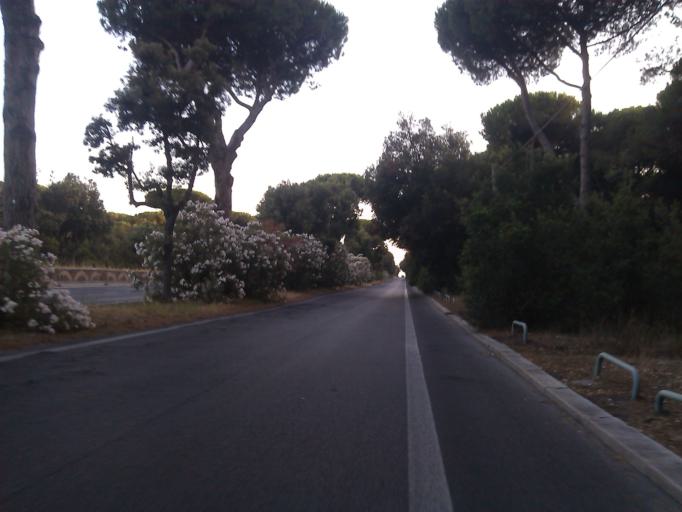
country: IT
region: Latium
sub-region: Citta metropolitana di Roma Capitale
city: Acilia-Castel Fusano-Ostia Antica
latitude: 41.7201
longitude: 12.3242
